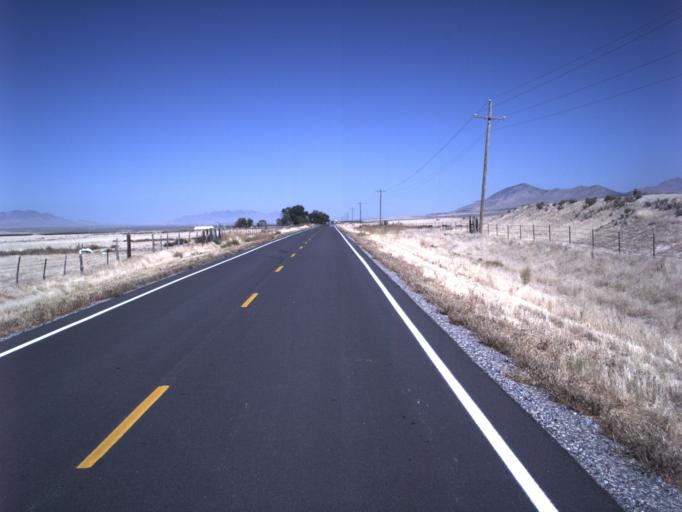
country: US
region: Utah
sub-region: Tooele County
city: Grantsville
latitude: 40.4253
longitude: -112.7488
